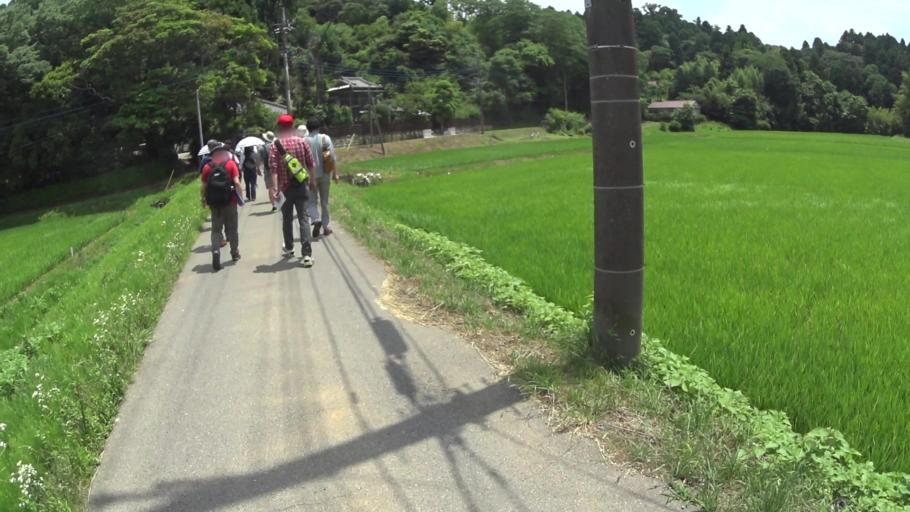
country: JP
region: Chiba
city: Sawara
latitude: 35.8899
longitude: 140.5272
